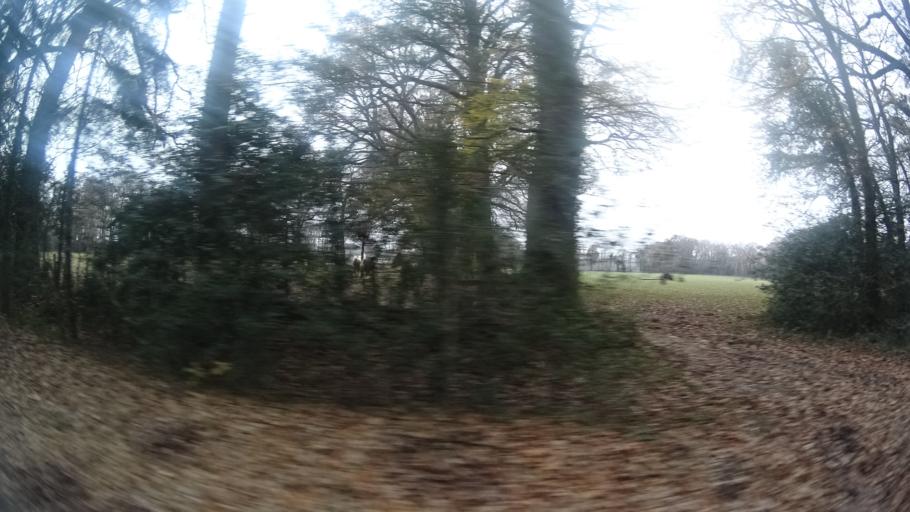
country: FR
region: Brittany
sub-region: Departement d'Ille-et-Vilaine
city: Bains-sur-Oust
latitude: 47.7069
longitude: -2.0516
